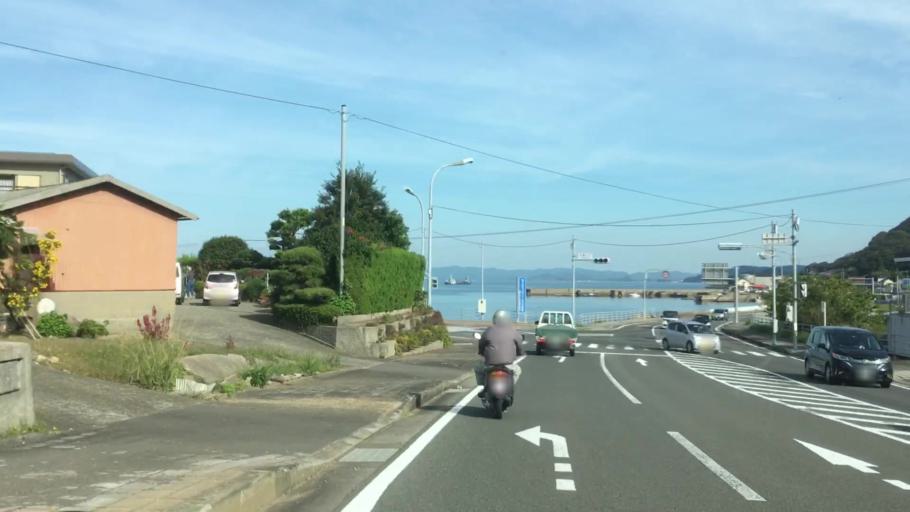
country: JP
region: Nagasaki
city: Sasebo
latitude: 33.0387
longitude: 129.6593
